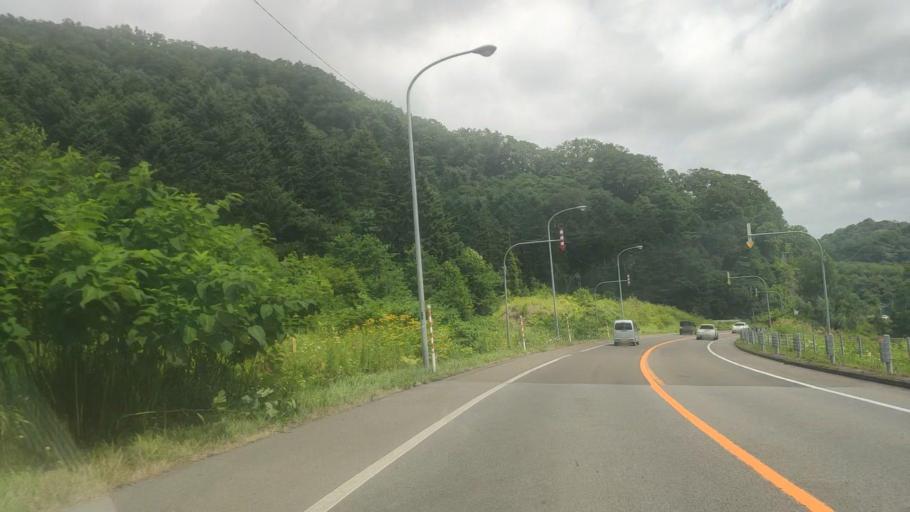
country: JP
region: Hokkaido
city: Niseko Town
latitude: 42.6044
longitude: 140.5612
